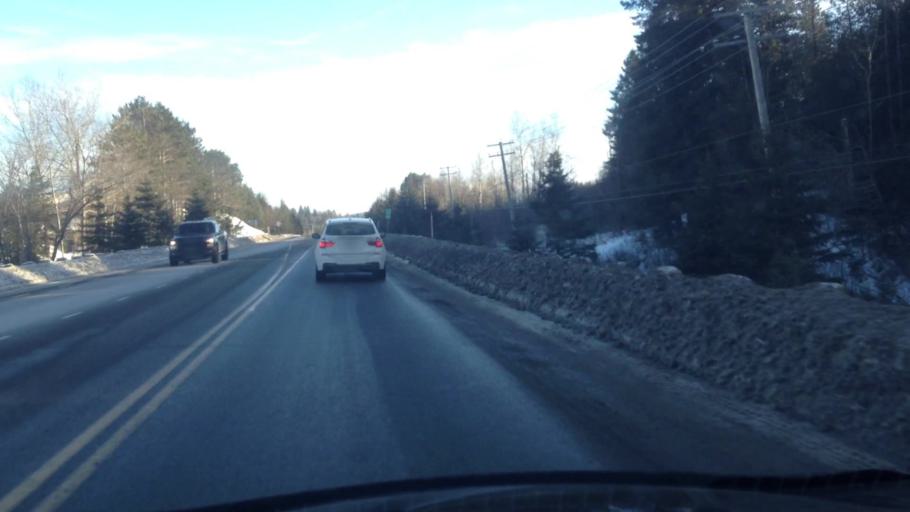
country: CA
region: Quebec
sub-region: Laurentides
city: Saint-Sauveur
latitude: 45.8955
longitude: -74.2027
